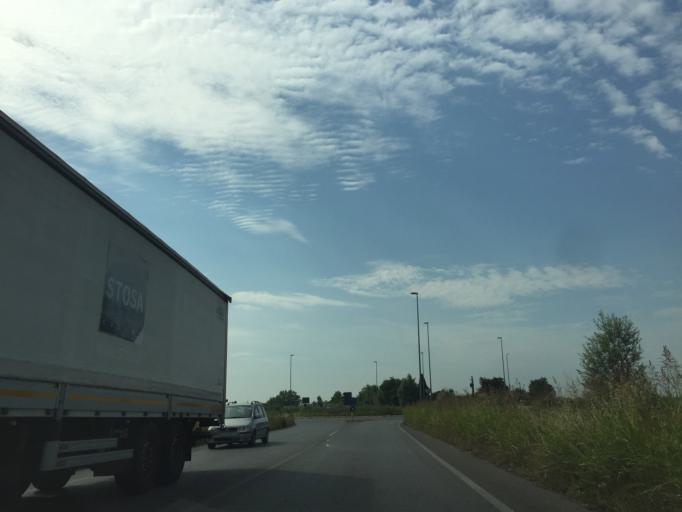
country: IT
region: Tuscany
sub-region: Provincia di Pistoia
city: Cintolese
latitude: 43.8396
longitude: 10.8206
